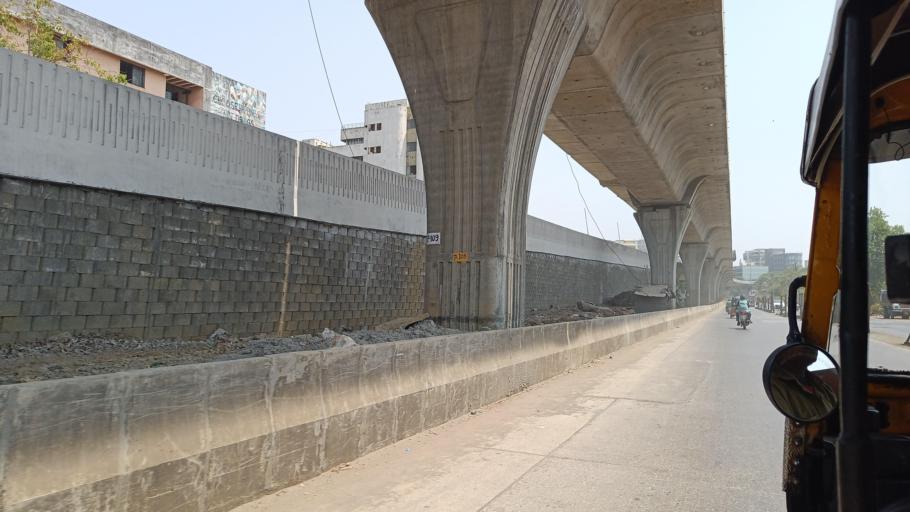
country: IN
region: Maharashtra
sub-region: Mumbai Suburban
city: Mumbai
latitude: 19.0758
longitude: 72.8564
